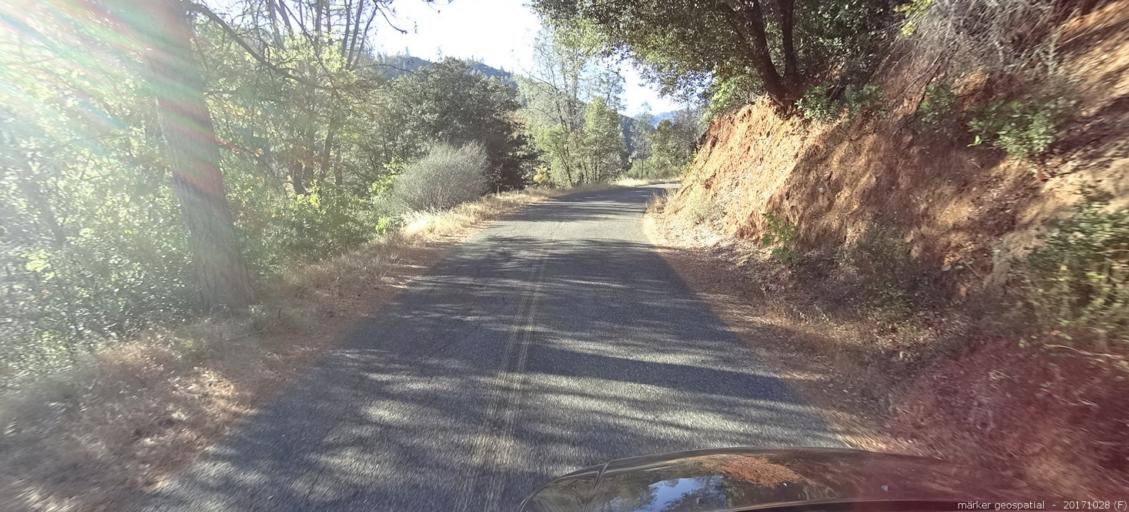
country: US
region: California
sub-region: Trinity County
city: Lewiston
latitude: 40.6660
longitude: -122.6539
